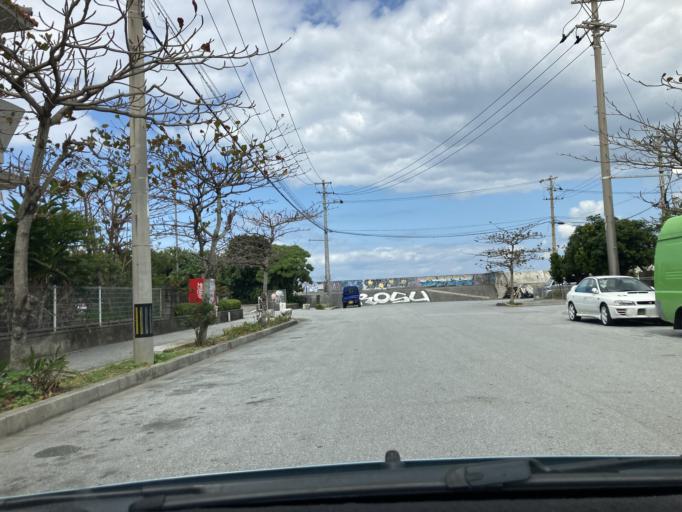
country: JP
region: Okinawa
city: Naha-shi
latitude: 26.2501
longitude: 127.6732
